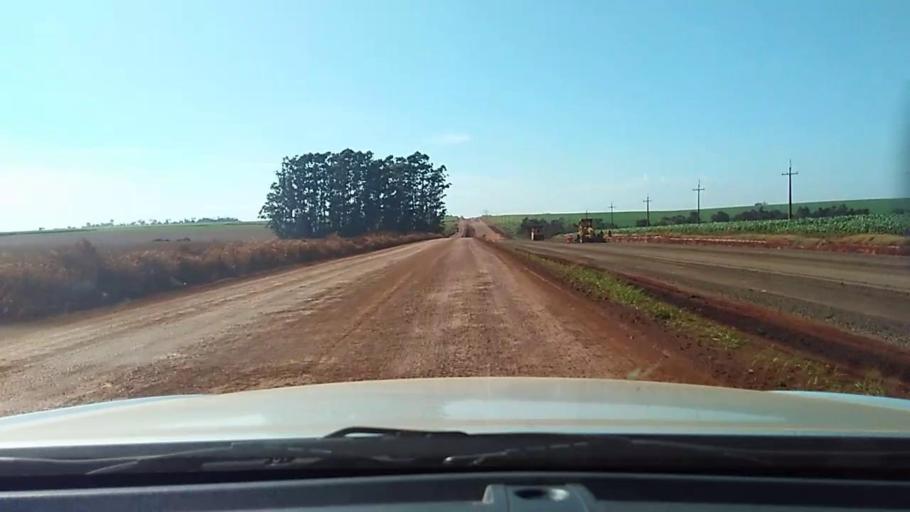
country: PY
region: Alto Parana
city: Naranjal
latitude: -25.9187
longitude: -55.4256
